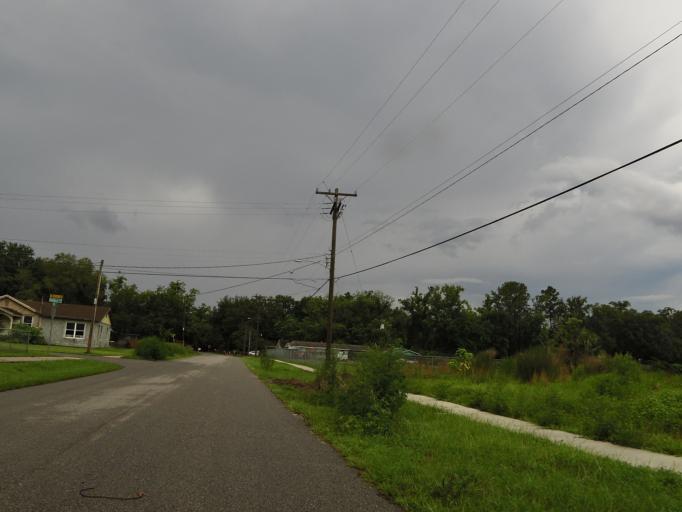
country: US
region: Florida
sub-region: Duval County
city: Jacksonville
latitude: 30.2787
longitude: -81.6385
